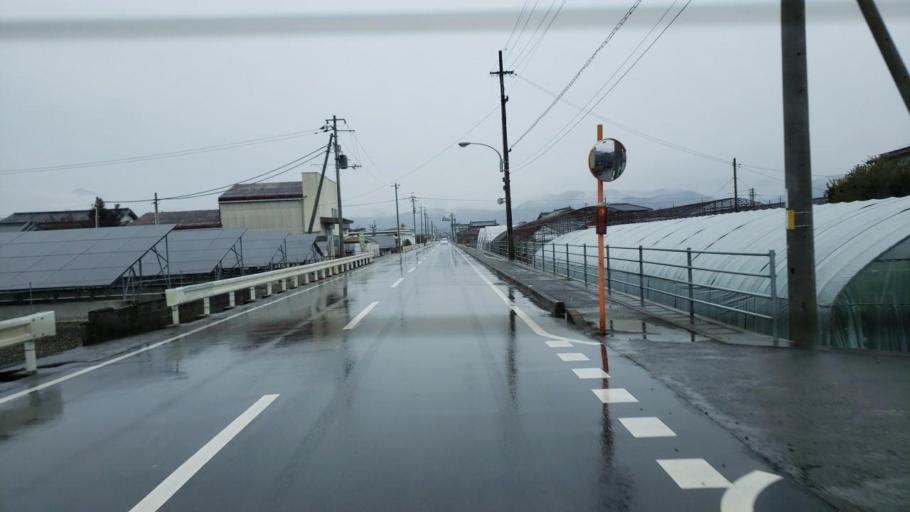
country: JP
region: Tokushima
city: Kamojimacho-jogejima
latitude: 34.0774
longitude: 134.2812
